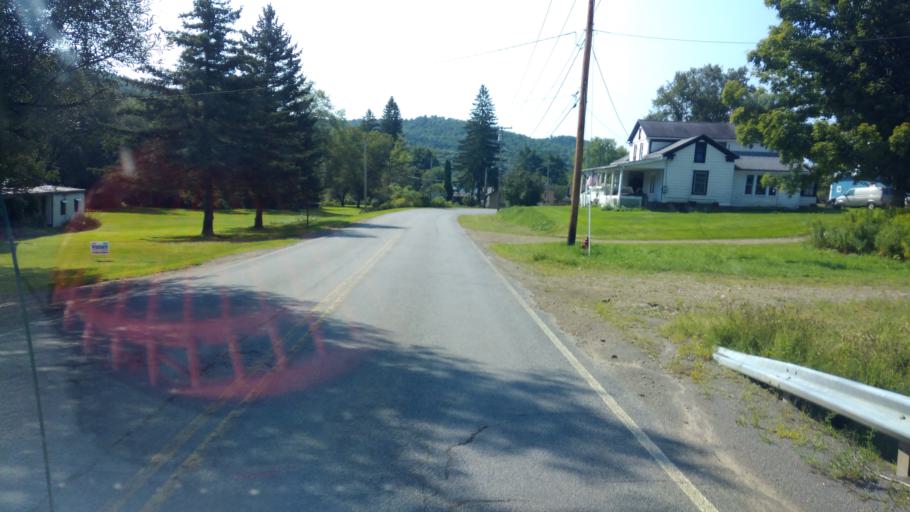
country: US
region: New York
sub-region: Allegany County
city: Bolivar
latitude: 42.0916
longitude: -78.1557
